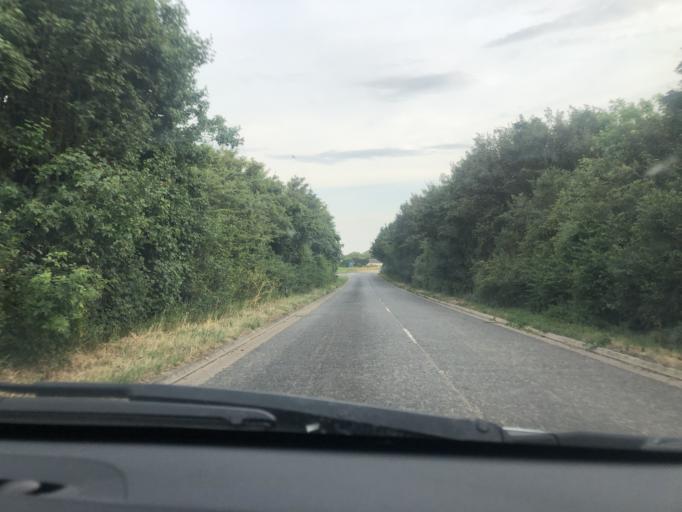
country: GB
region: England
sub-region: Kent
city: Herne Bay
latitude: 51.3593
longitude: 1.1692
